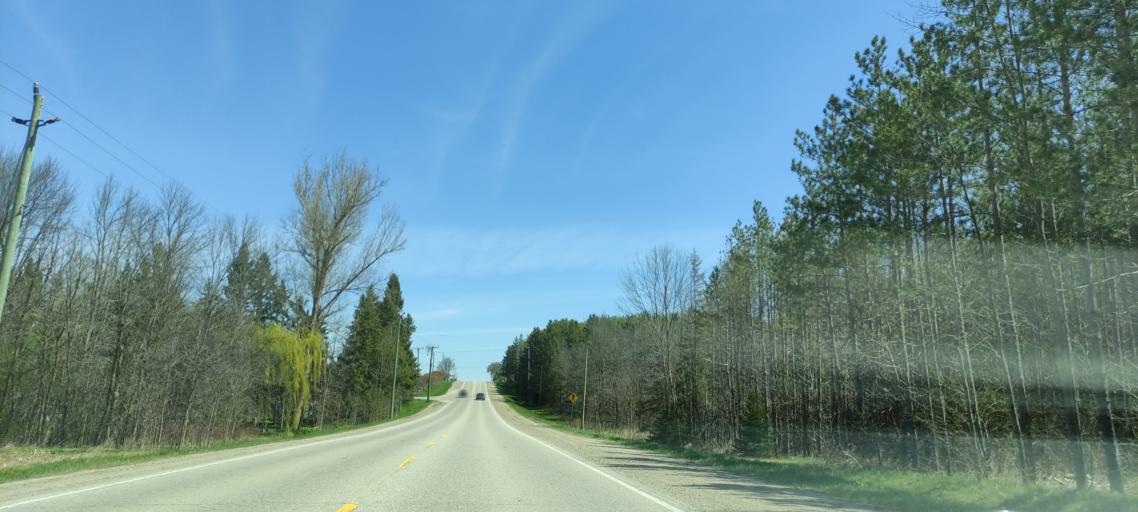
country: CA
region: Ontario
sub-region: Wellington County
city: Guelph
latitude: 43.5868
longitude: -80.3536
